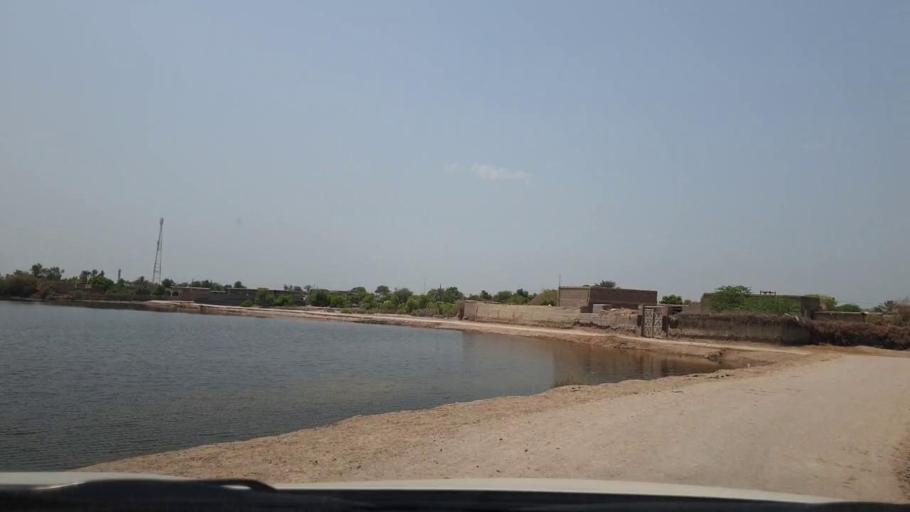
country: PK
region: Sindh
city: Radhan
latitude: 27.2477
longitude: 67.9925
